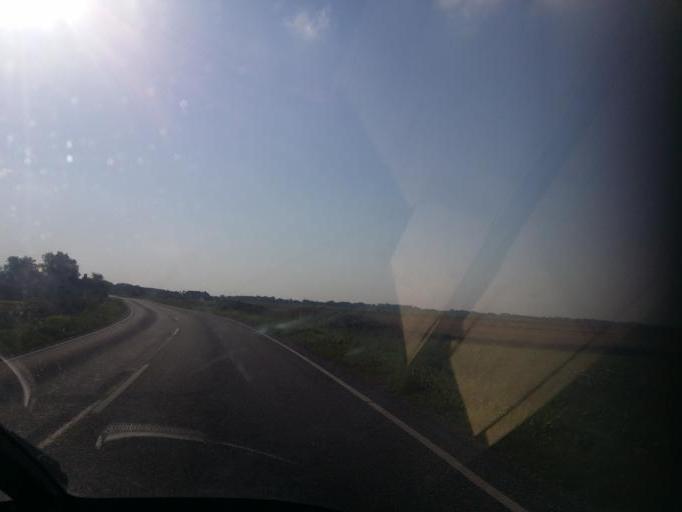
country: DE
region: Schleswig-Holstein
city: Rodenas
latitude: 54.9169
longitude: 8.7325
